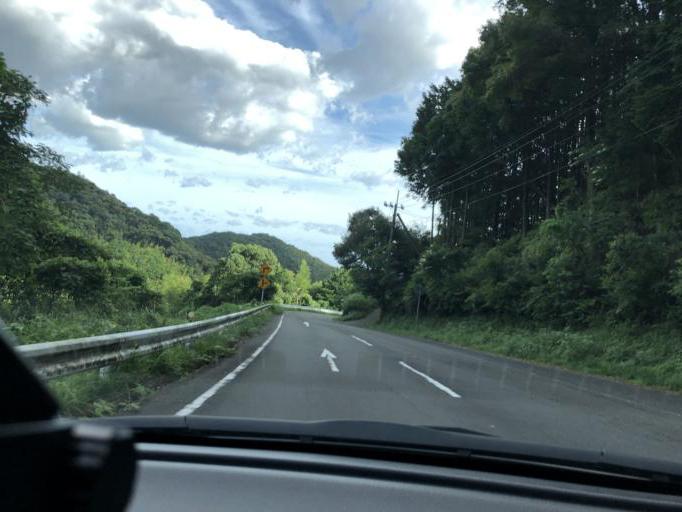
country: JP
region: Kochi
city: Kochi-shi
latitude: 33.5976
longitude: 133.5090
